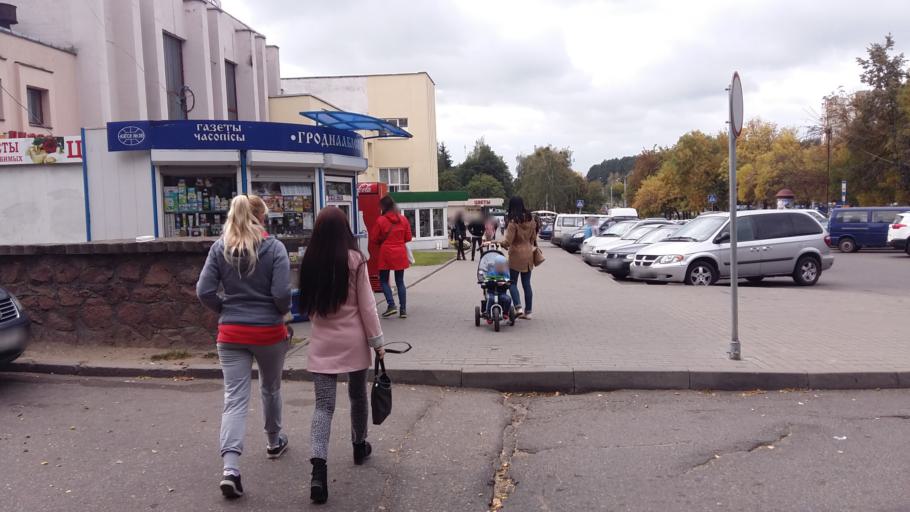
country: BY
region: Grodnenskaya
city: Hrodna
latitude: 53.6973
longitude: 23.8055
